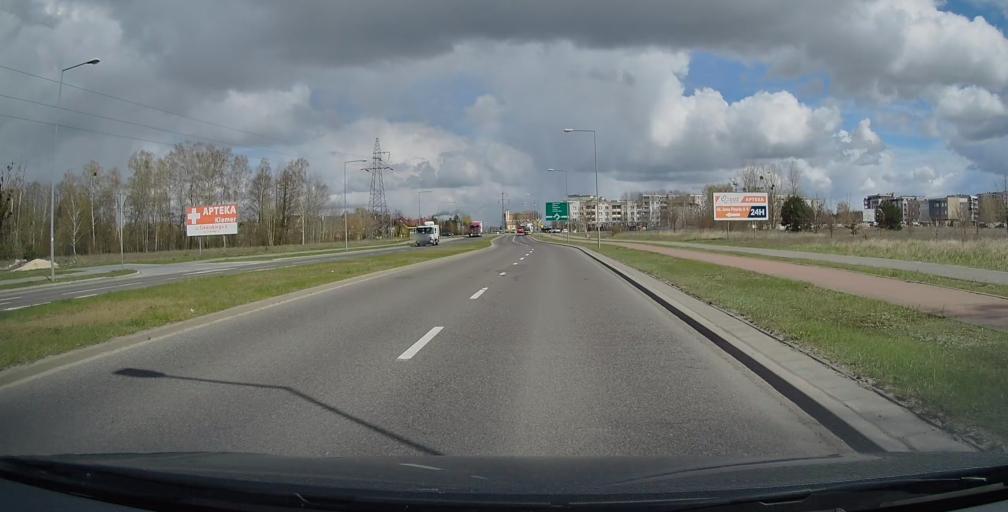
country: PL
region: Masovian Voivodeship
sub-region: Ostroleka
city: Ostroleka
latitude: 53.0663
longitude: 21.5892
